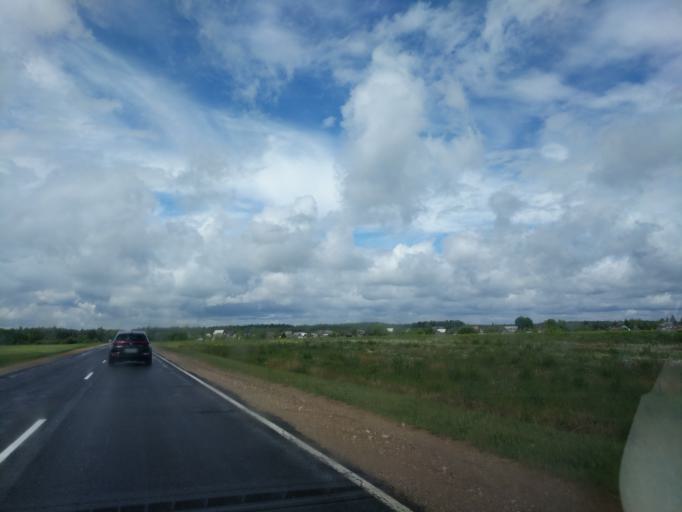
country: BY
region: Minsk
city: Il'ya
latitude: 54.3940
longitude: 27.3426
